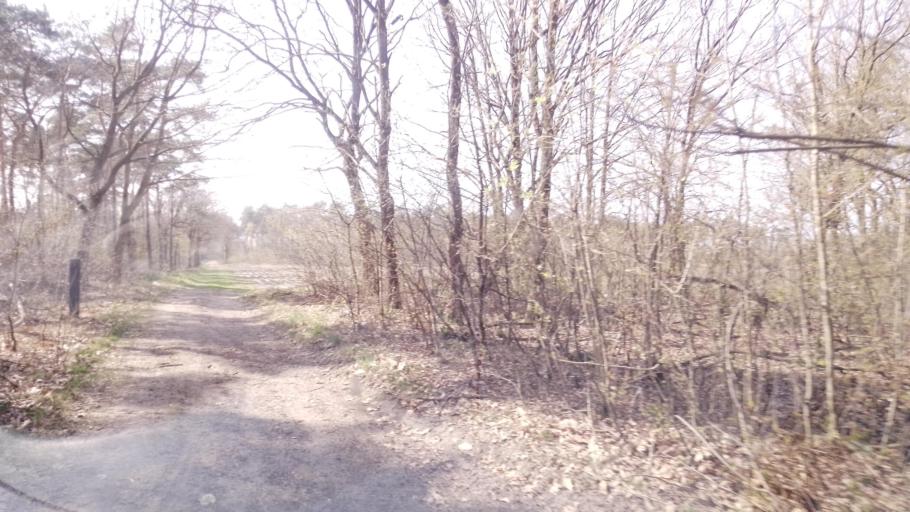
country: NL
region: Limburg
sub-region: Gemeente Peel en Maas
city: Maasbree
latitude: 51.3810
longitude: 6.0742
